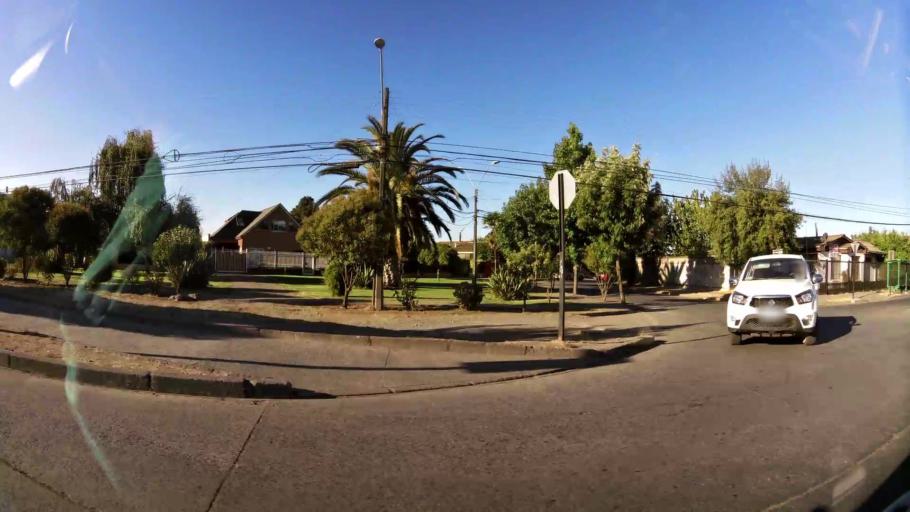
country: CL
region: Maule
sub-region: Provincia de Curico
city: Curico
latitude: -34.9756
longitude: -71.2188
